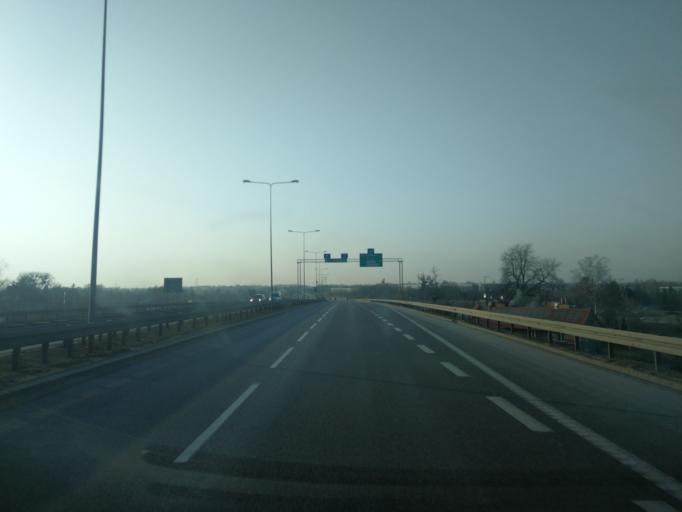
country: PL
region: Warmian-Masurian Voivodeship
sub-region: Powiat elblaski
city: Elblag
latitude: 54.1447
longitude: 19.3894
